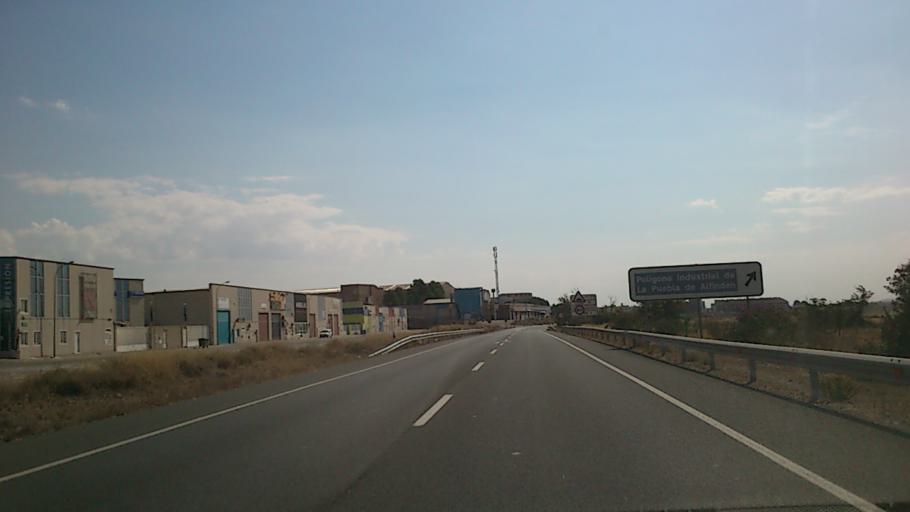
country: ES
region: Aragon
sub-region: Provincia de Zaragoza
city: Puebla de Alfinden
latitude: 41.6400
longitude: -0.7671
